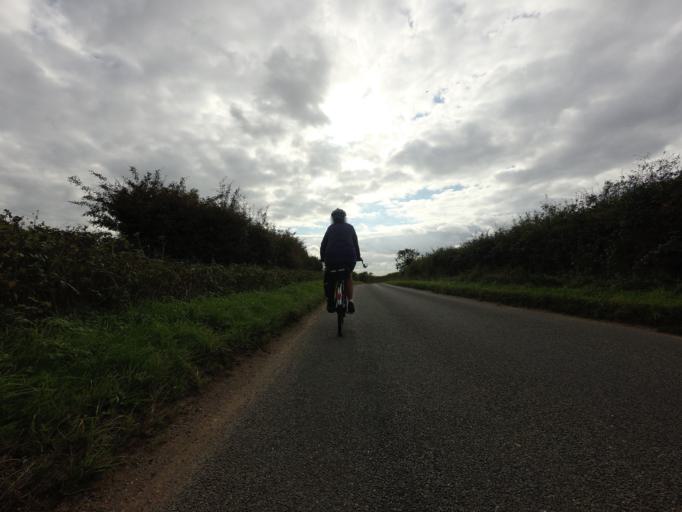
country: GB
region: England
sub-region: Norfolk
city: Snettisham
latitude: 52.8822
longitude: 0.5199
